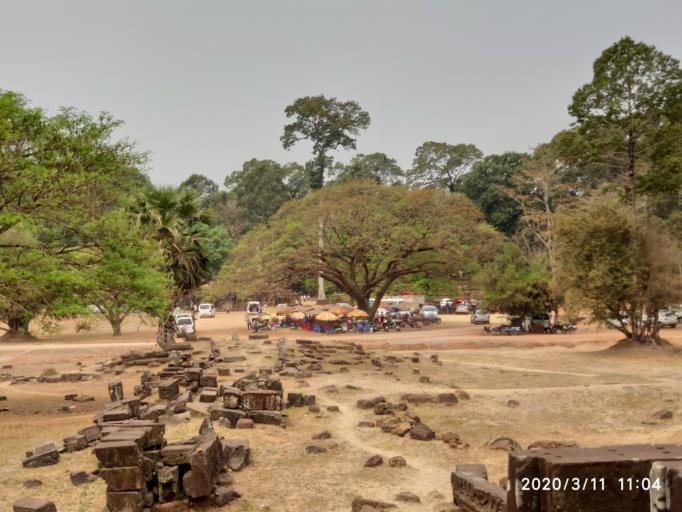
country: KH
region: Siem Reap
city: Siem Reap
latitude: 13.4472
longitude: 103.8609
